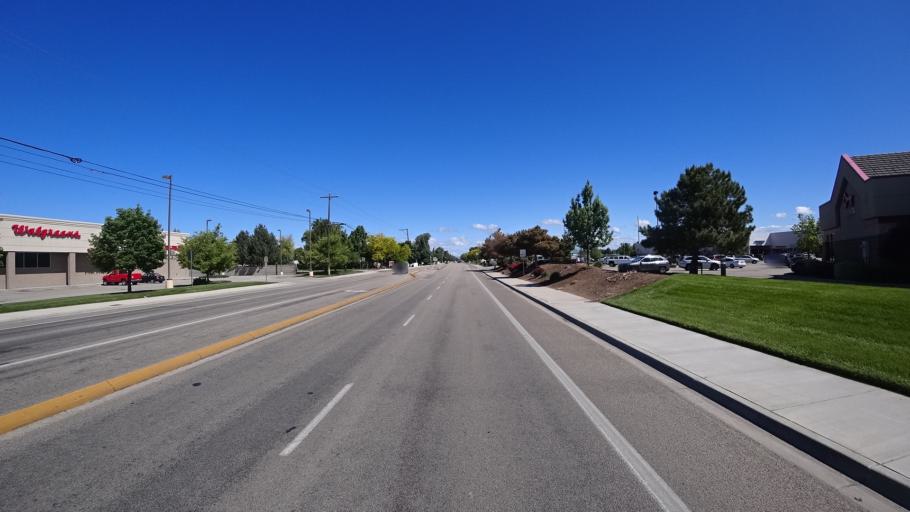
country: US
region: Idaho
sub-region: Ada County
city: Meridian
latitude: 43.6199
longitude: -116.3745
